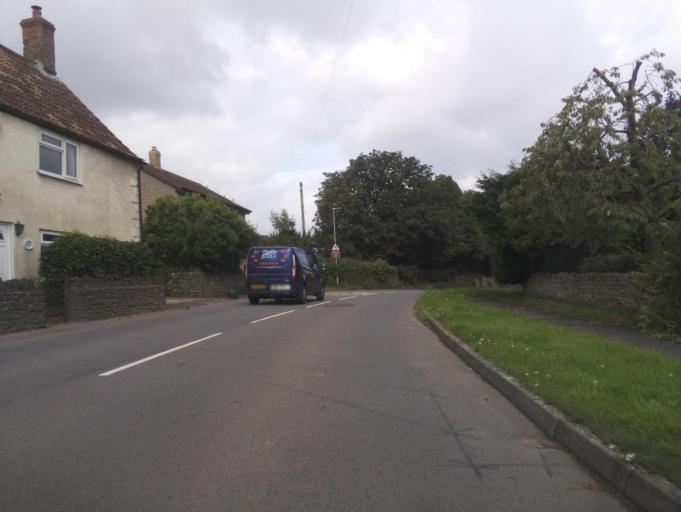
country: GB
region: England
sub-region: Dorset
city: Stalbridge
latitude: 50.9893
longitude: -2.4078
